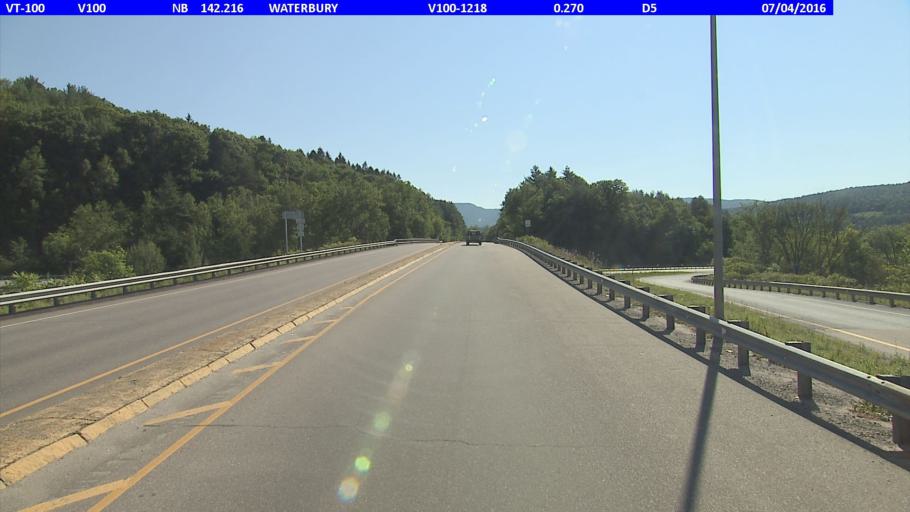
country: US
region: Vermont
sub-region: Washington County
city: Waterbury
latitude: 44.3430
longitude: -72.7541
